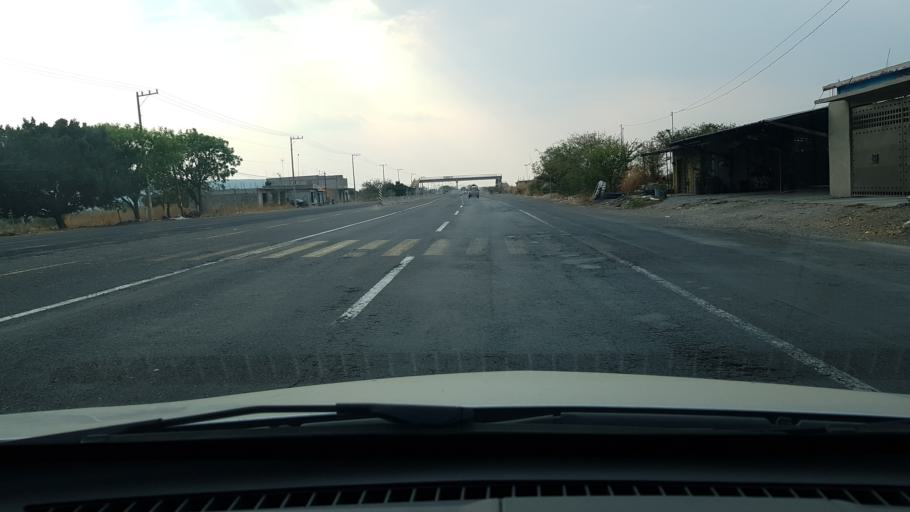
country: MX
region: Morelos
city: Amayuca
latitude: 18.7372
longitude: -98.8241
